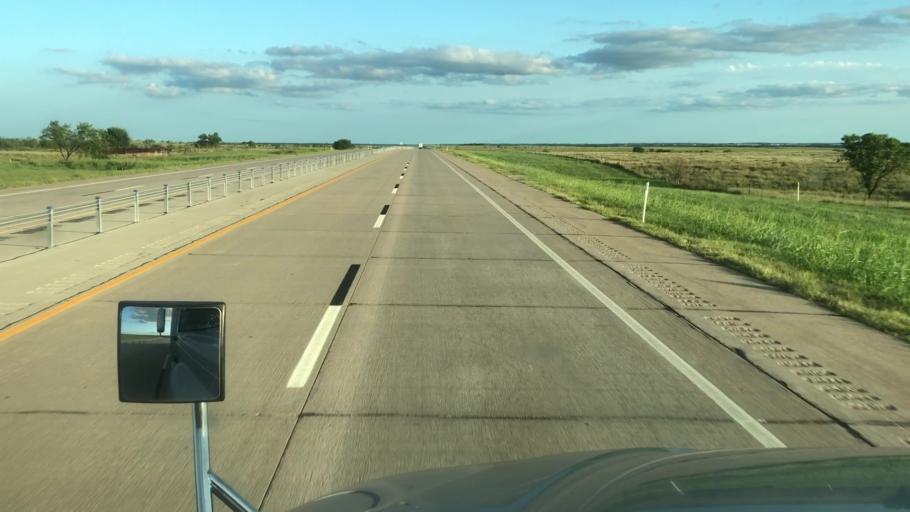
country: US
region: Oklahoma
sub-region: Pawnee County
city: Pawnee
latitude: 36.3639
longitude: -97.0341
